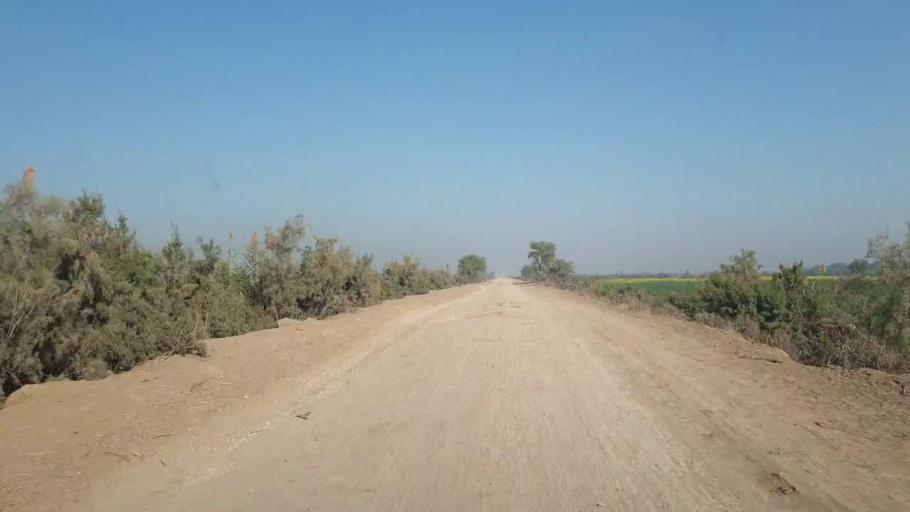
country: PK
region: Sindh
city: Shahdadpur
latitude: 25.9700
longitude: 68.4984
